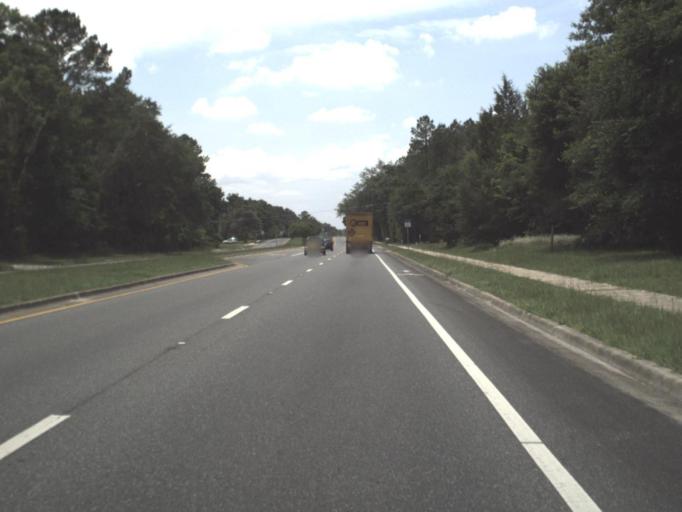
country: US
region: Florida
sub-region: Alachua County
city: Newberry
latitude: 29.6542
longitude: -82.5260
